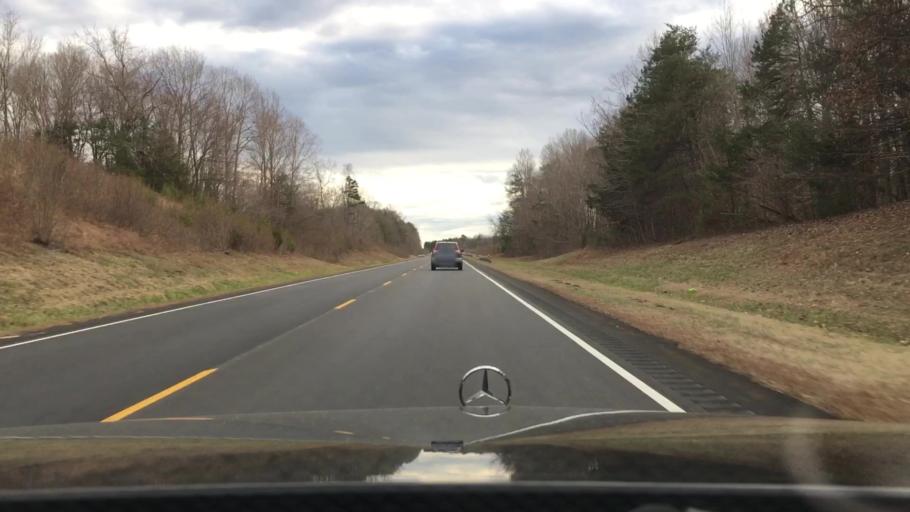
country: US
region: North Carolina
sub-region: Caswell County
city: Yanceyville
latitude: 36.3097
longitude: -79.2187
